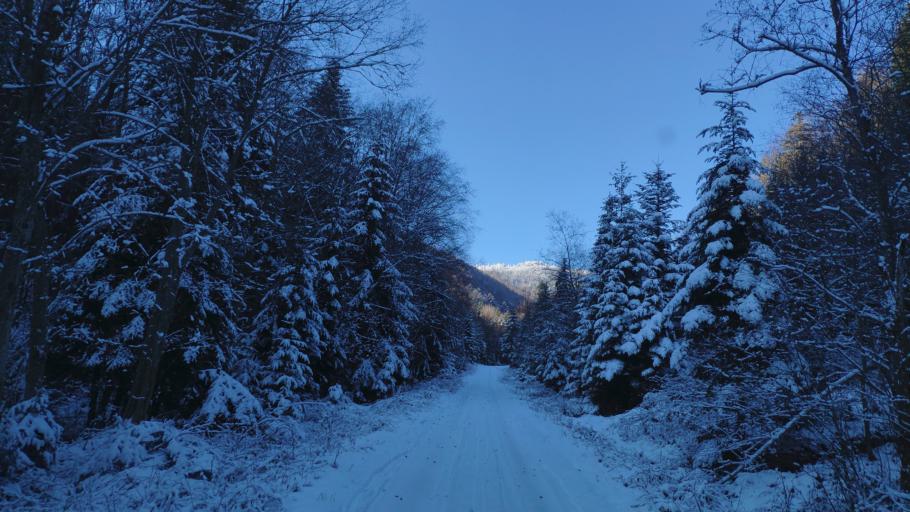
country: SK
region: Kosicky
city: Medzev
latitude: 48.7633
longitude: 20.9678
